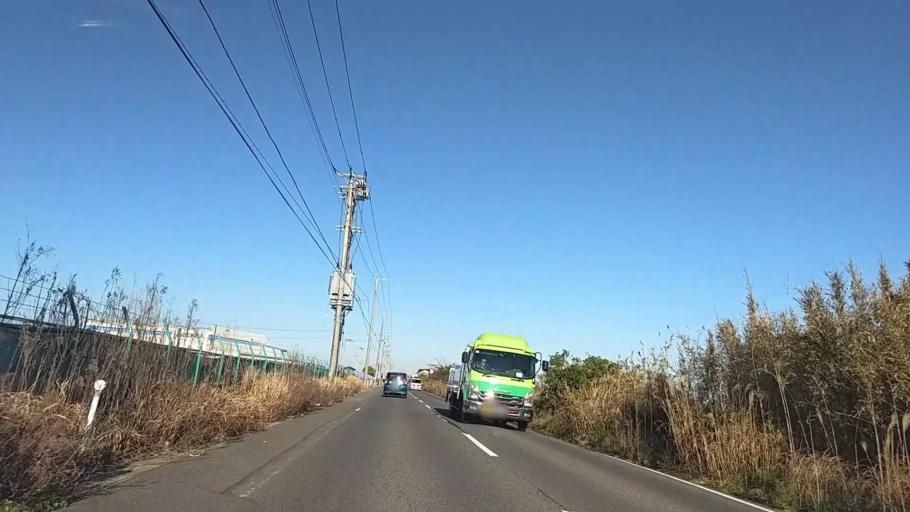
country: JP
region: Chiba
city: Asahi
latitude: 35.6733
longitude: 140.6206
